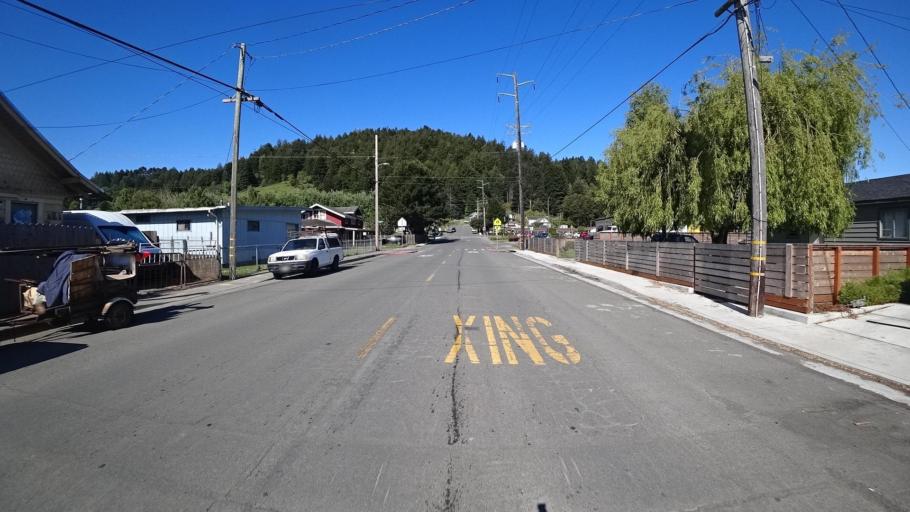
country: US
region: California
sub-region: Humboldt County
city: Rio Dell
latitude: 40.4993
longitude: -124.1046
